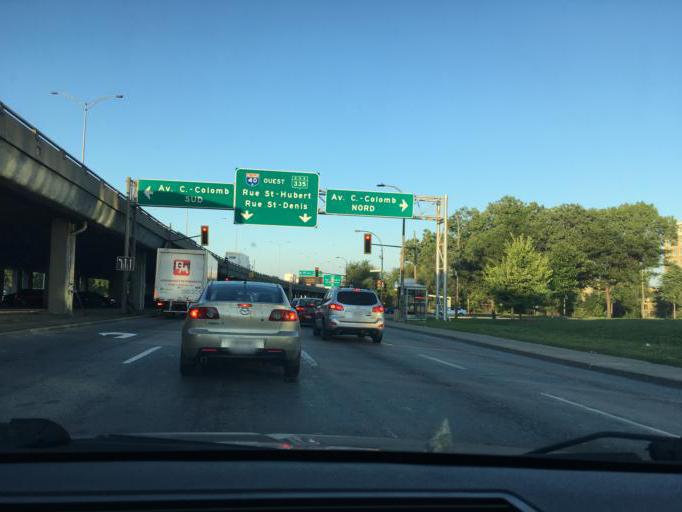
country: CA
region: Quebec
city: Mont-Royal
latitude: 45.5511
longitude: -73.6293
